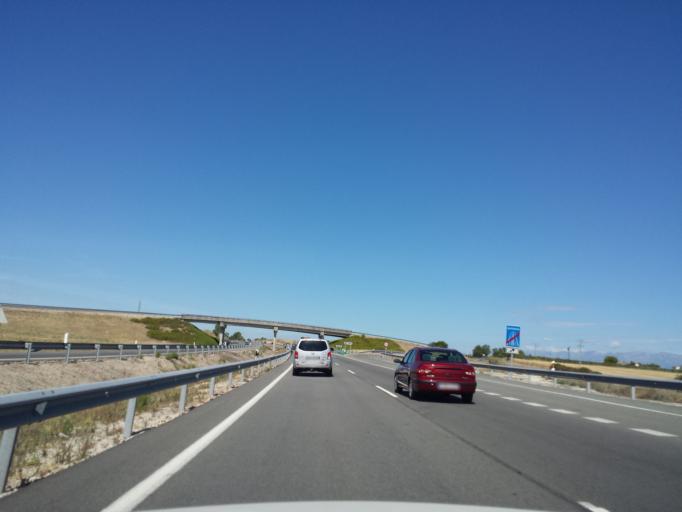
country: ES
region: Castille-La Mancha
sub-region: Province of Toledo
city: Torralba de Oropesa
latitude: 39.9306
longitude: -5.1409
